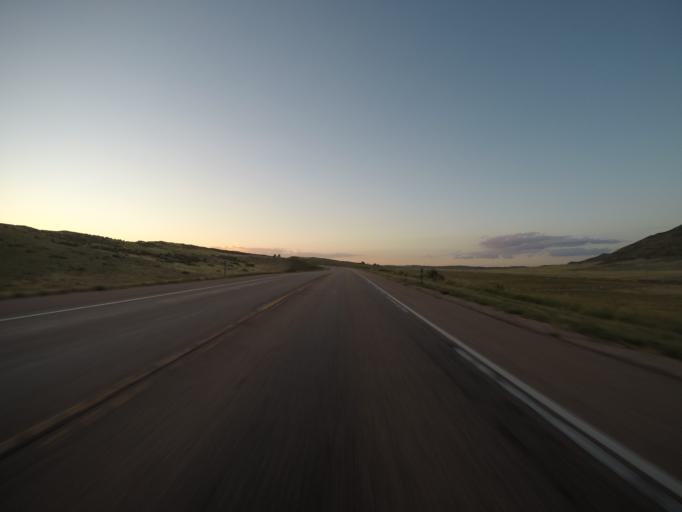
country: US
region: Colorado
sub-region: Larimer County
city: Laporte
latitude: 40.7544
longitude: -105.1710
